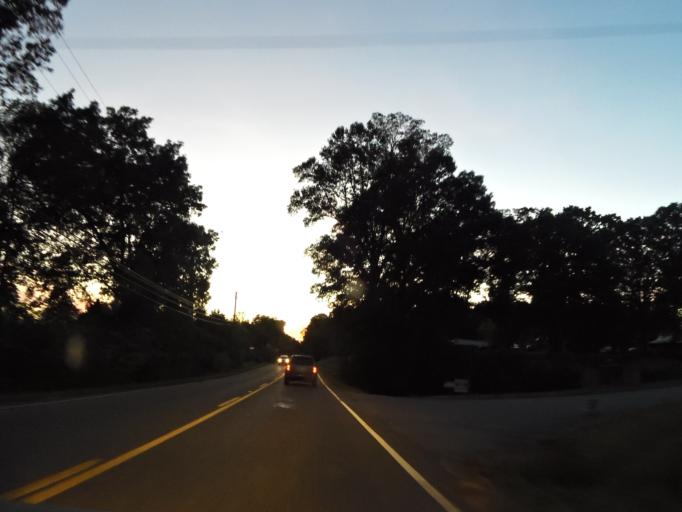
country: US
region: Tennessee
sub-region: Knox County
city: Mascot
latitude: 36.0190
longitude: -83.6651
